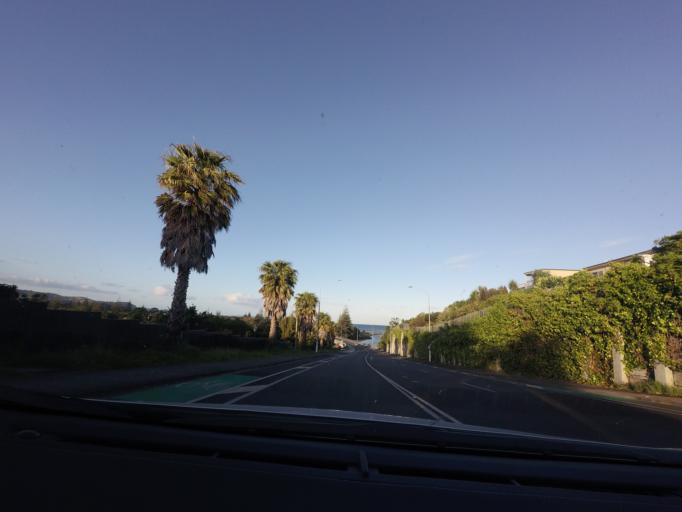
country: NZ
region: Auckland
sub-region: Auckland
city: Rothesay Bay
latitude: -36.6012
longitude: 174.6955
